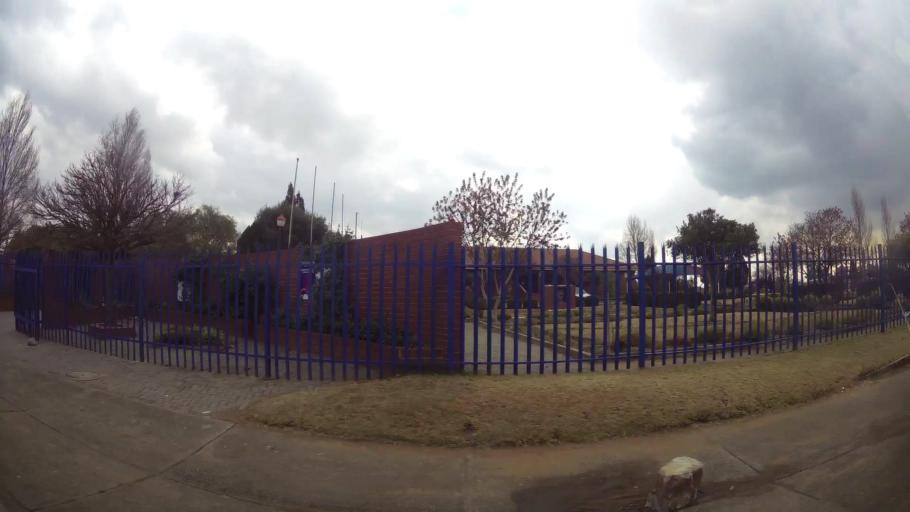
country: ZA
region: Orange Free State
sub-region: Fezile Dabi District Municipality
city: Sasolburg
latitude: -26.8513
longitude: 27.8776
